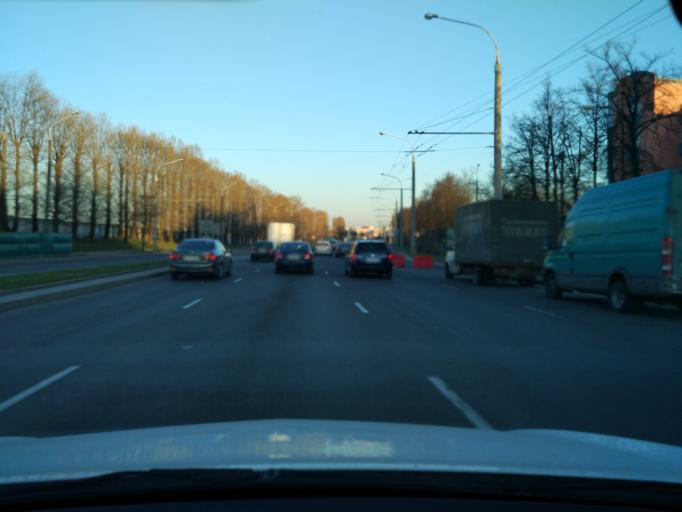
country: BY
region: Minsk
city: Syenitsa
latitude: 53.8670
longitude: 27.5270
